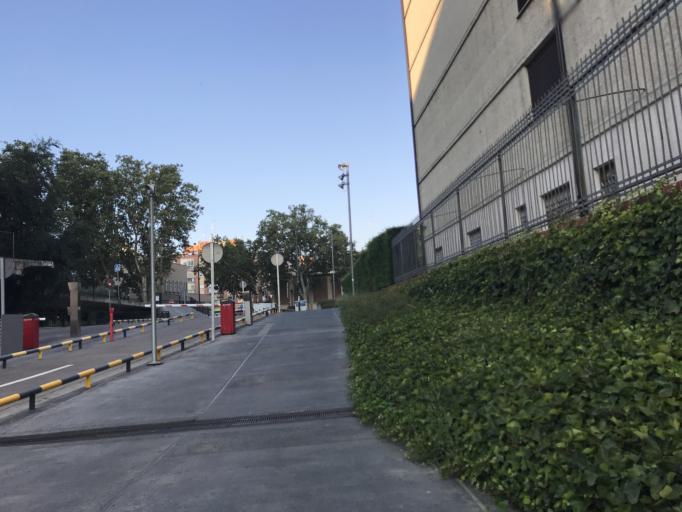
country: ES
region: Castille and Leon
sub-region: Provincia de Valladolid
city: Valladolid
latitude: 41.6564
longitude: -4.7195
